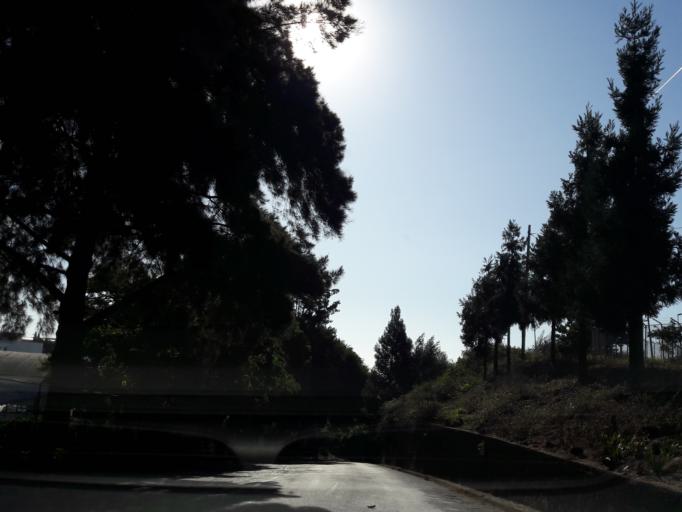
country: PT
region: Madeira
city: Canico
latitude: 32.6514
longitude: -16.8631
